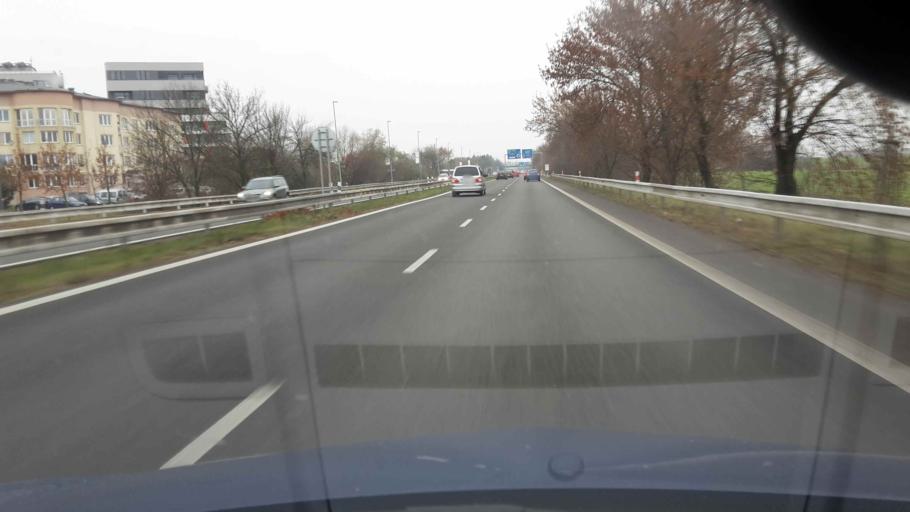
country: CZ
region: Olomoucky
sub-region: Okres Olomouc
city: Olomouc
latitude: 49.5999
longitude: 17.2298
